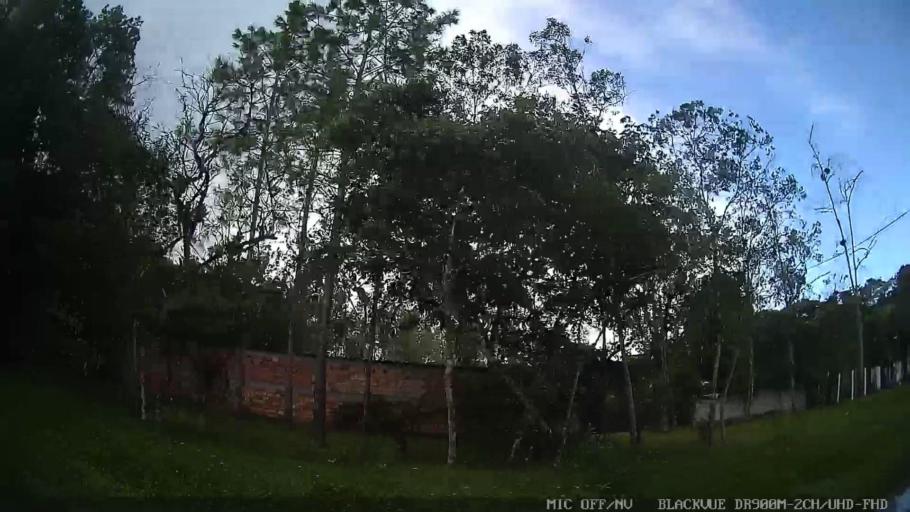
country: BR
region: Sao Paulo
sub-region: Peruibe
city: Peruibe
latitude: -24.1979
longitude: -46.9403
